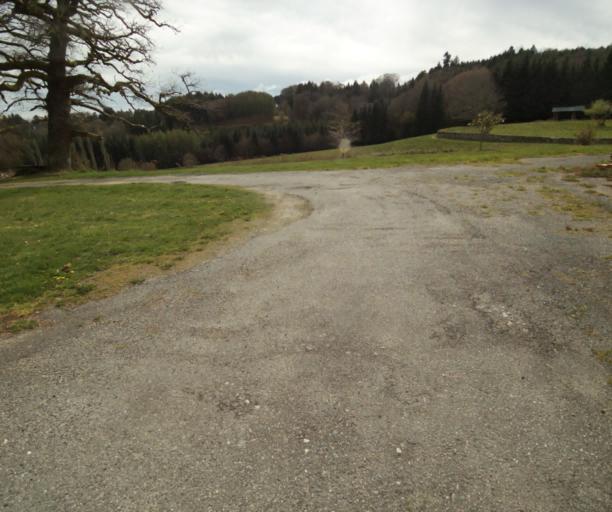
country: FR
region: Limousin
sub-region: Departement de la Correze
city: Argentat
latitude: 45.2027
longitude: 1.9683
